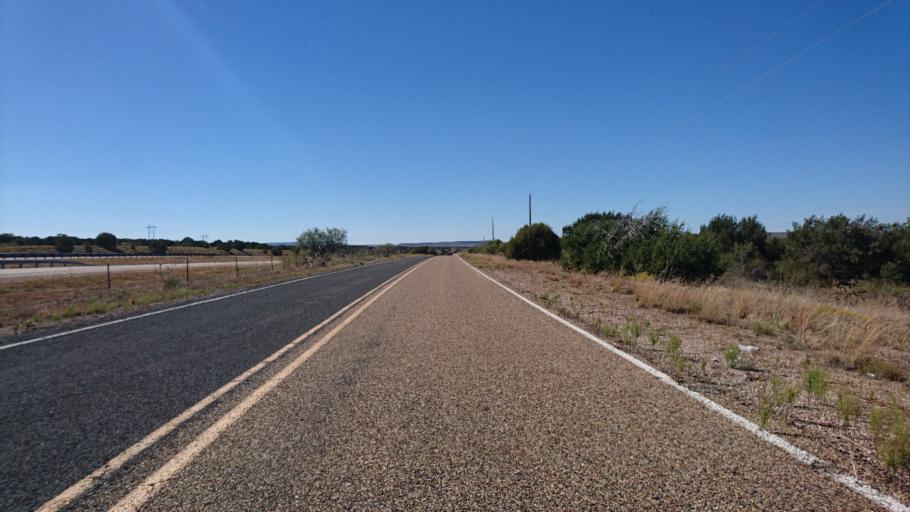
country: US
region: New Mexico
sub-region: Quay County
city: Tucumcari
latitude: 35.0668
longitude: -104.1852
